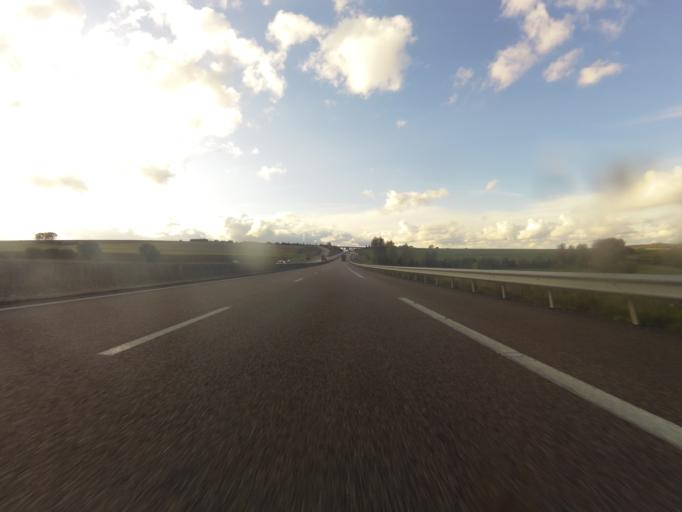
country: FR
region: Haute-Normandie
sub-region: Departement de la Seine-Maritime
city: Neufchatel-en-Bray
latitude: 49.7404
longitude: 1.5389
